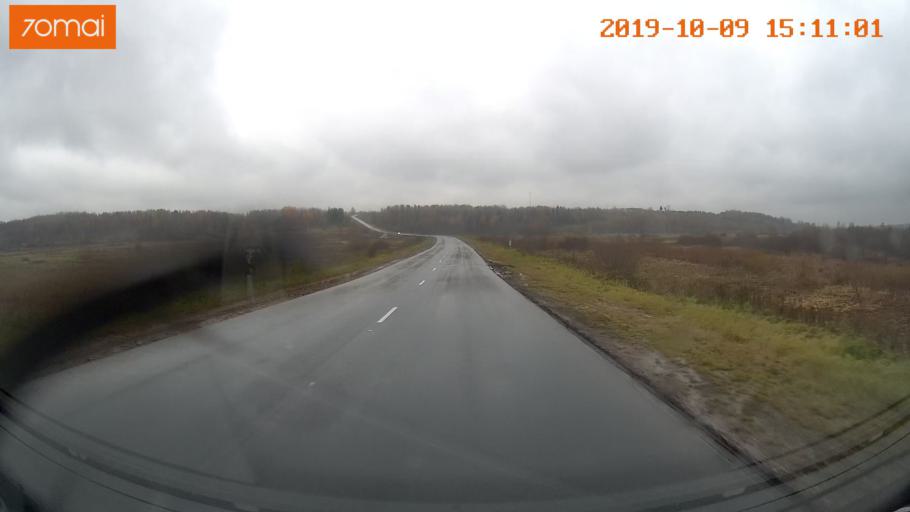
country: RU
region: Kostroma
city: Susanino
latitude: 58.1708
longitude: 41.6333
